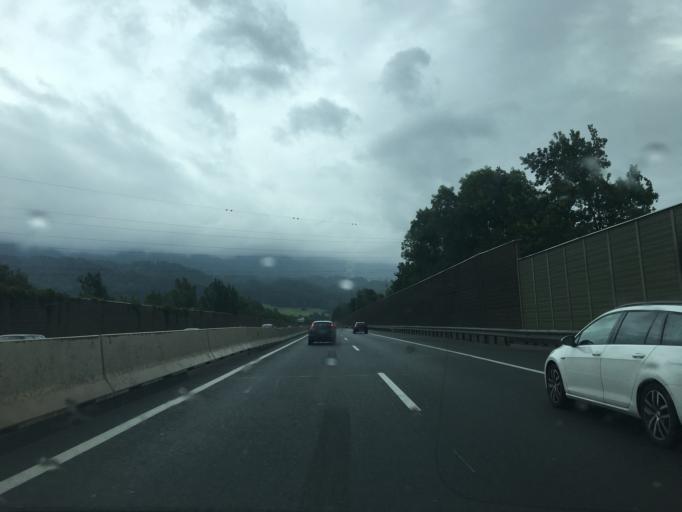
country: AT
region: Tyrol
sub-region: Politischer Bezirk Innsbruck Land
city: Volders
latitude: 47.2889
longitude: 11.5603
